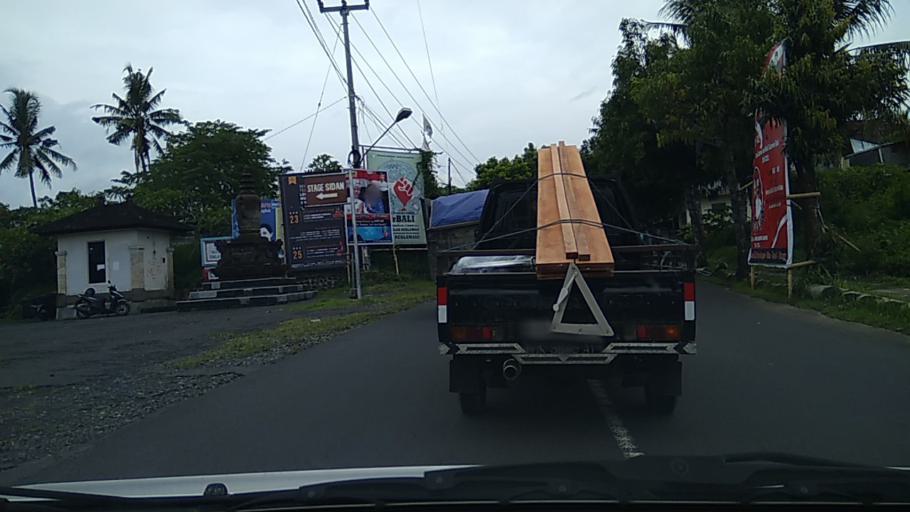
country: ID
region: Bali
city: Banjar Kelodan
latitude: -8.5348
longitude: 115.3475
